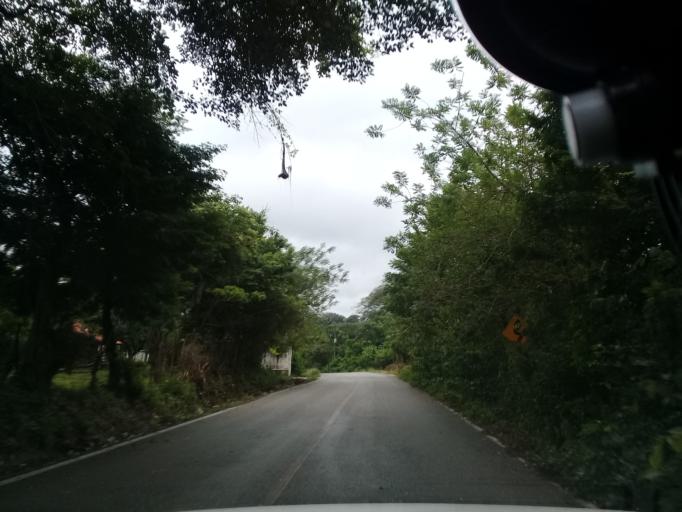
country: MX
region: Veracruz
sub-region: Chalma
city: San Pedro Coyutla
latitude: 21.2091
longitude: -98.4087
